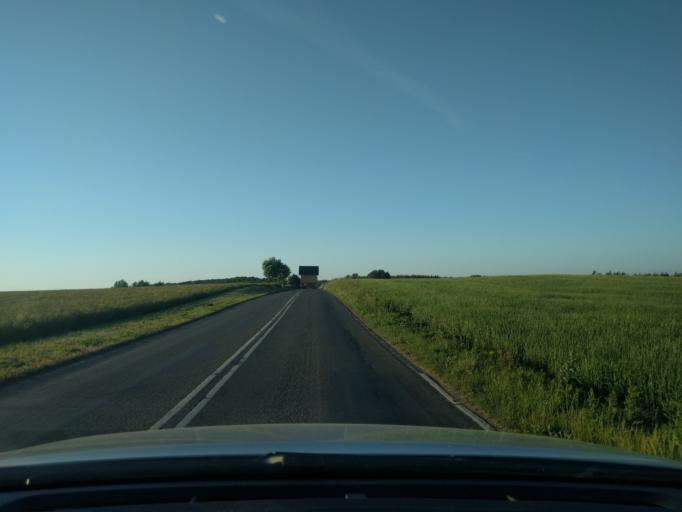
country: DK
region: South Denmark
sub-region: Kerteminde Kommune
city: Kerteminde
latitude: 55.5668
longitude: 10.6462
